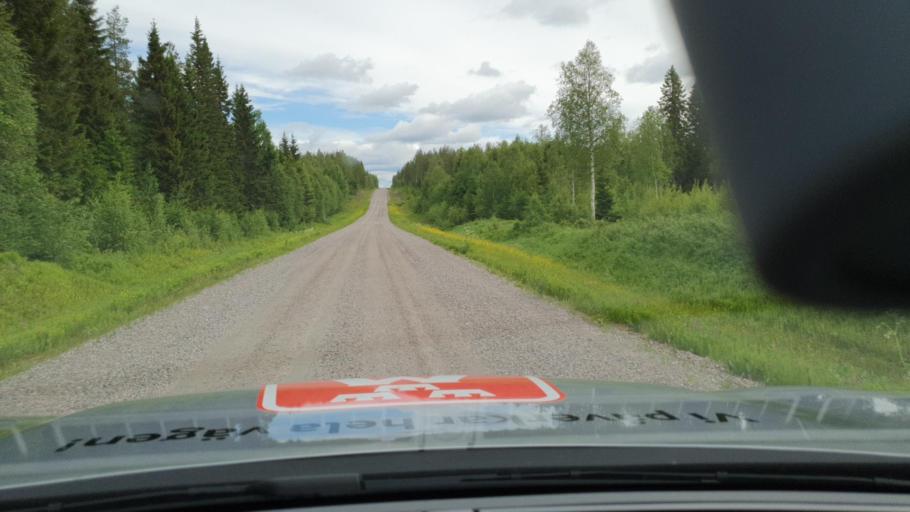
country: FI
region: Lapland
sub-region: Torniolaakso
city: Ylitornio
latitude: 65.9973
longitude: 23.8023
